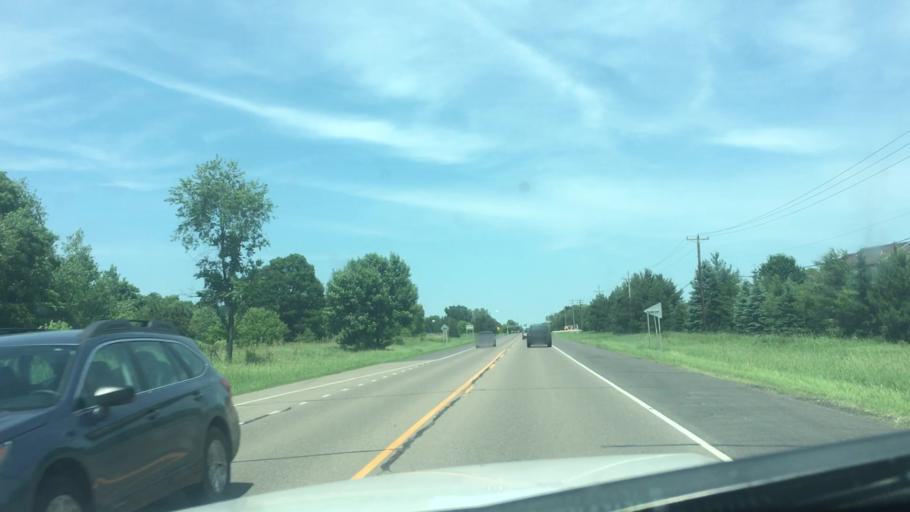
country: US
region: Minnesota
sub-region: Washington County
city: Hugo
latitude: 45.1319
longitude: -93.0015
